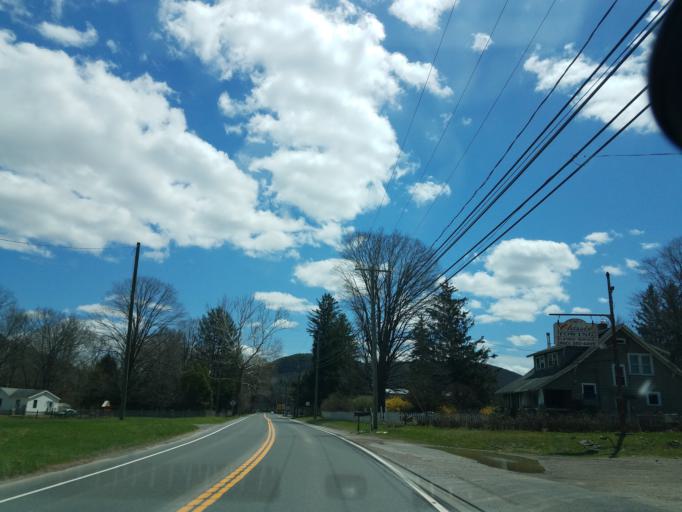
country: US
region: Connecticut
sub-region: Fairfield County
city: Sherman
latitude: 41.6421
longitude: -73.4841
